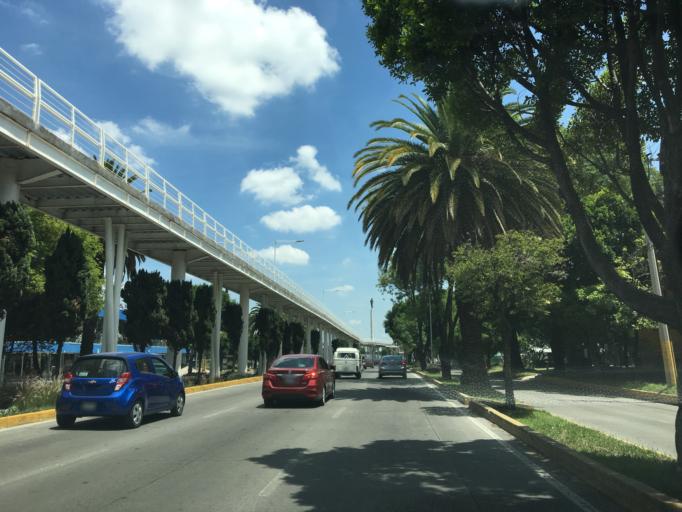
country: MX
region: Puebla
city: Puebla
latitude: 19.0610
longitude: -98.2204
